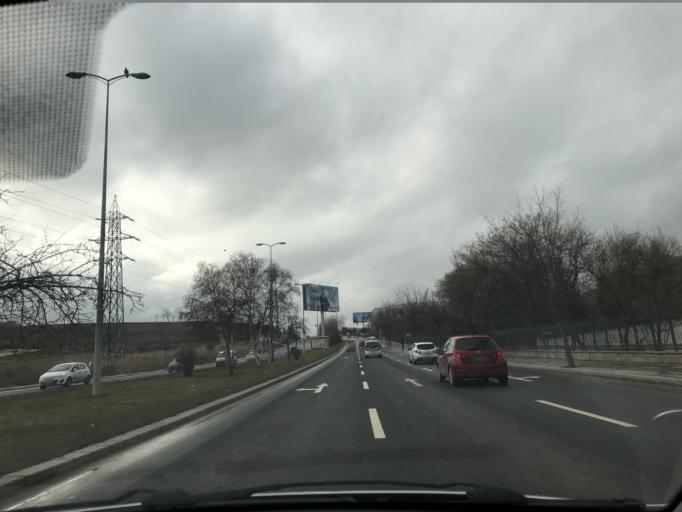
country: TR
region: Ankara
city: Batikent
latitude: 39.9593
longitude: 32.7844
